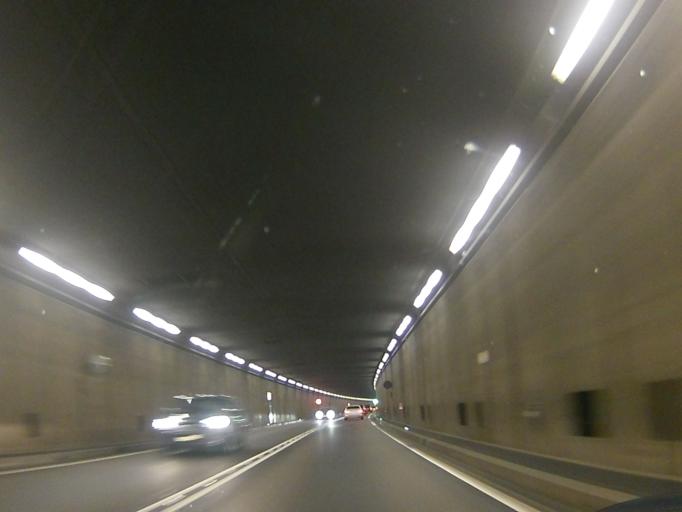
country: CH
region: Uri
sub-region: Uri
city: Andermatt
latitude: 46.5904
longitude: 8.5653
